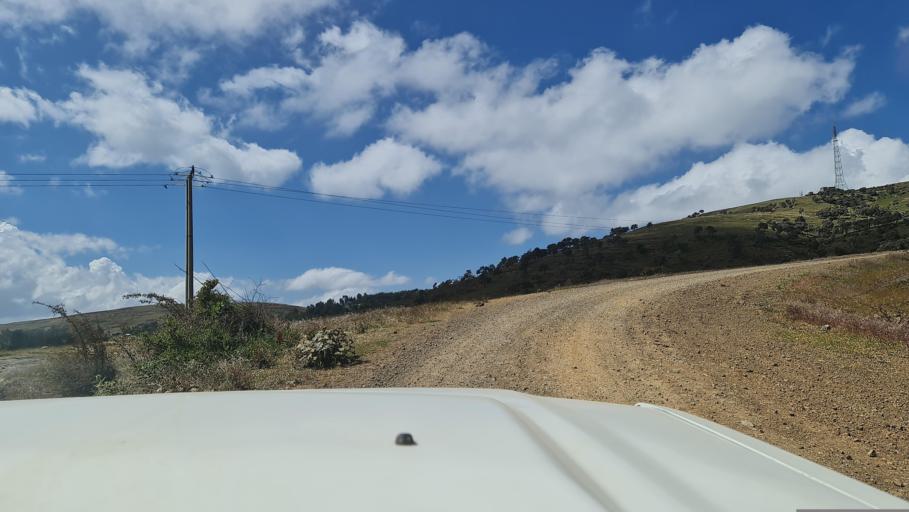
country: ET
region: Amhara
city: Debark'
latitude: 13.2046
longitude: 37.9859
